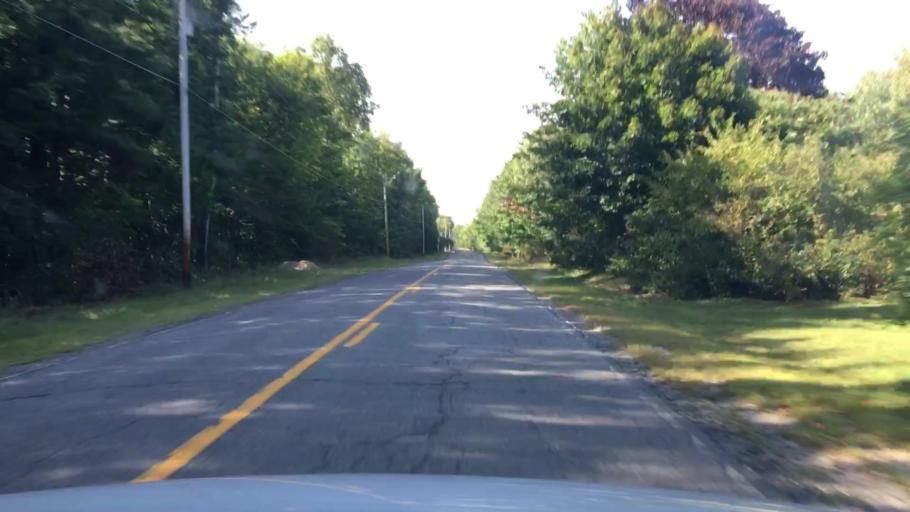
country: US
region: Maine
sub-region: Penobscot County
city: Enfield
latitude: 45.2196
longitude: -68.5359
